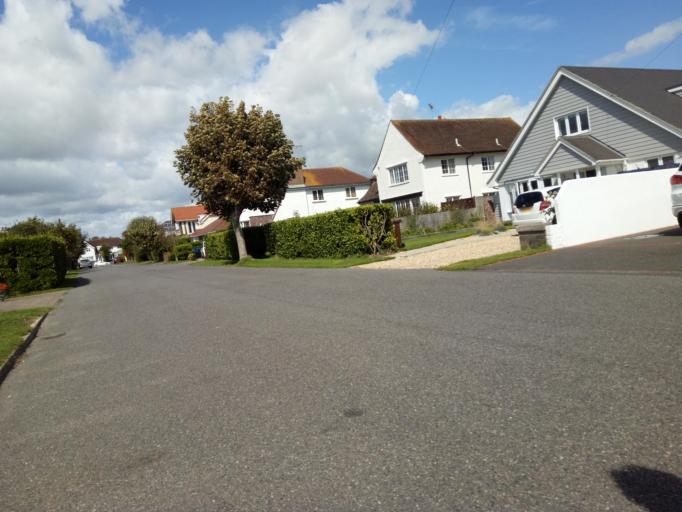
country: GB
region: England
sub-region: West Sussex
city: Bognor Regis
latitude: 50.7884
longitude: -0.6422
